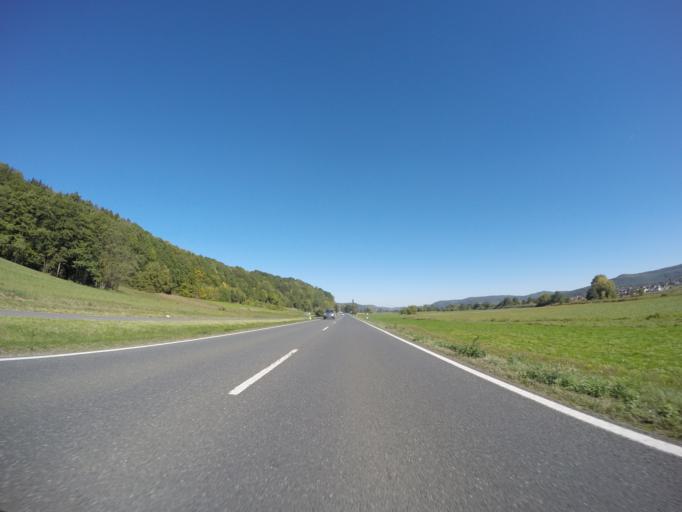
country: DE
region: Bavaria
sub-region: Upper Franconia
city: Wiesenthau
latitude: 49.7310
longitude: 11.1270
